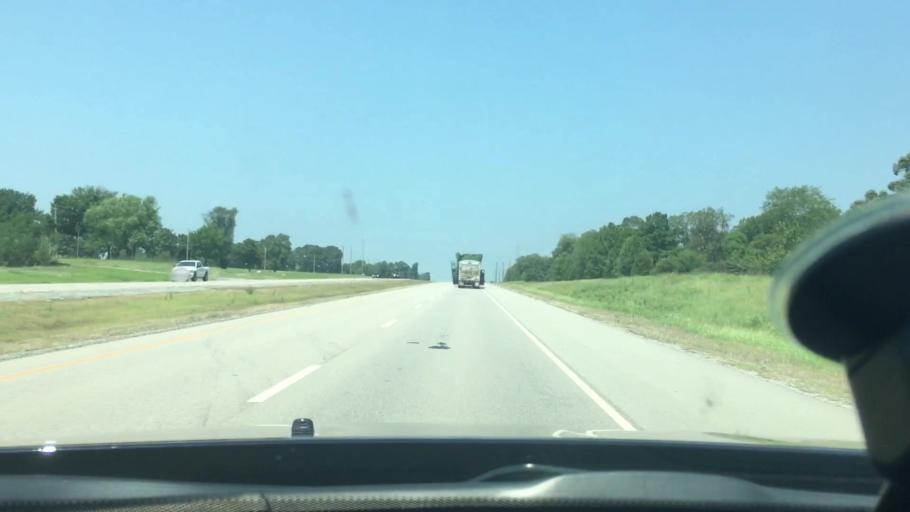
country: US
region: Oklahoma
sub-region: Atoka County
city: Atoka
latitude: 34.3257
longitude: -96.0432
